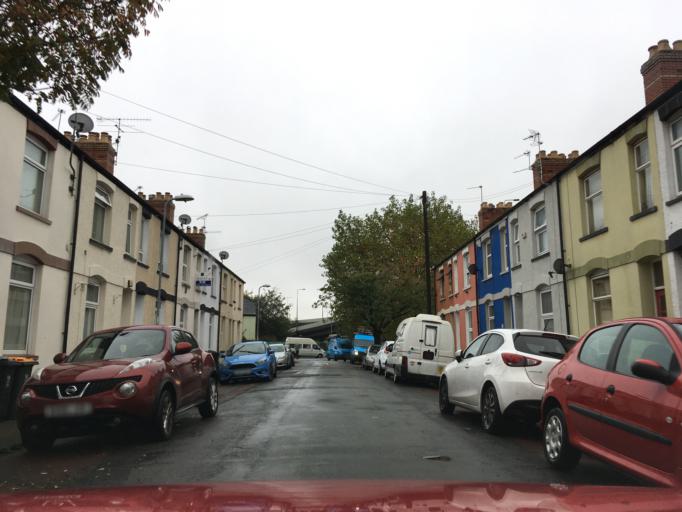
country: GB
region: Wales
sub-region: Newport
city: Newport
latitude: 51.5979
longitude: -2.9979
